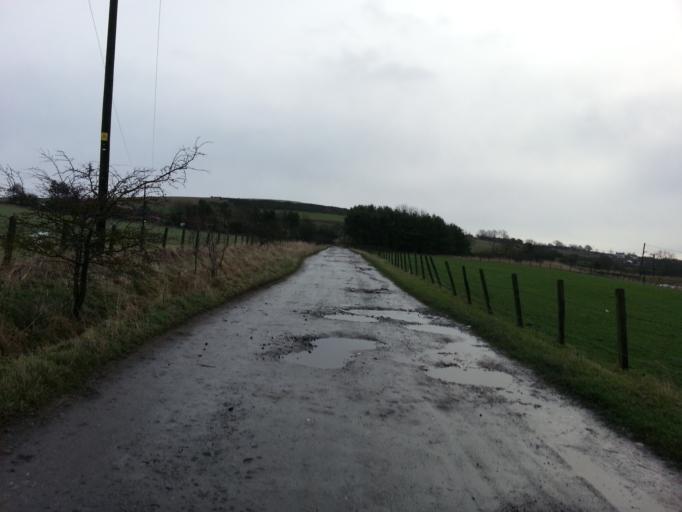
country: GB
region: England
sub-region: County Durham
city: Crook
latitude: 54.7264
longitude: -1.7476
